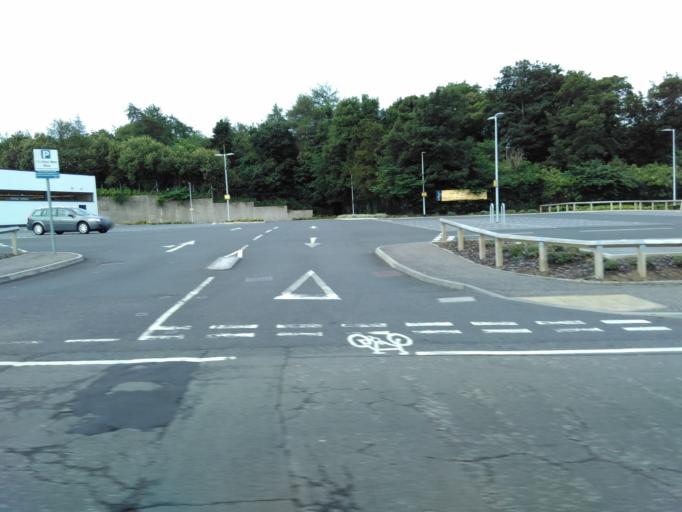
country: GB
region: Scotland
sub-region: Midlothian
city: Loanhead
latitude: 55.9134
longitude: -3.1468
